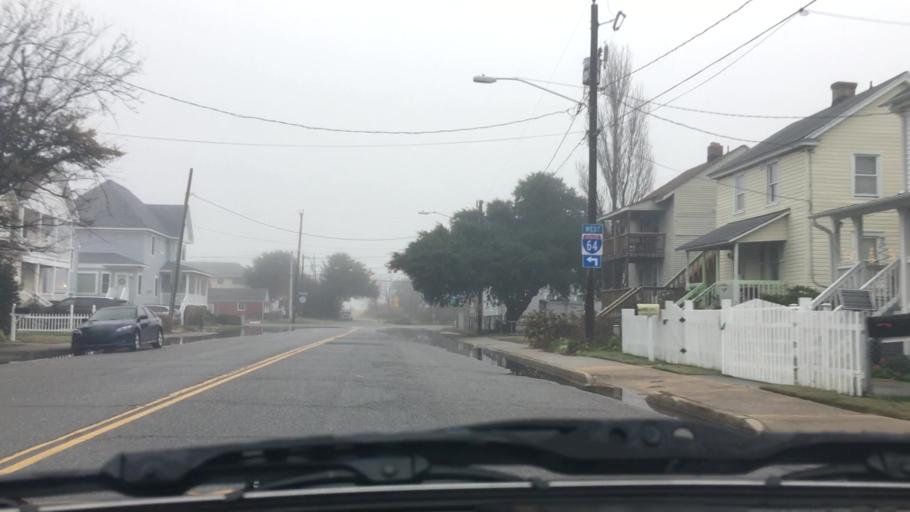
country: US
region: Virginia
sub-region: City of Hampton
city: East Hampton
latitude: 36.9663
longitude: -76.2880
